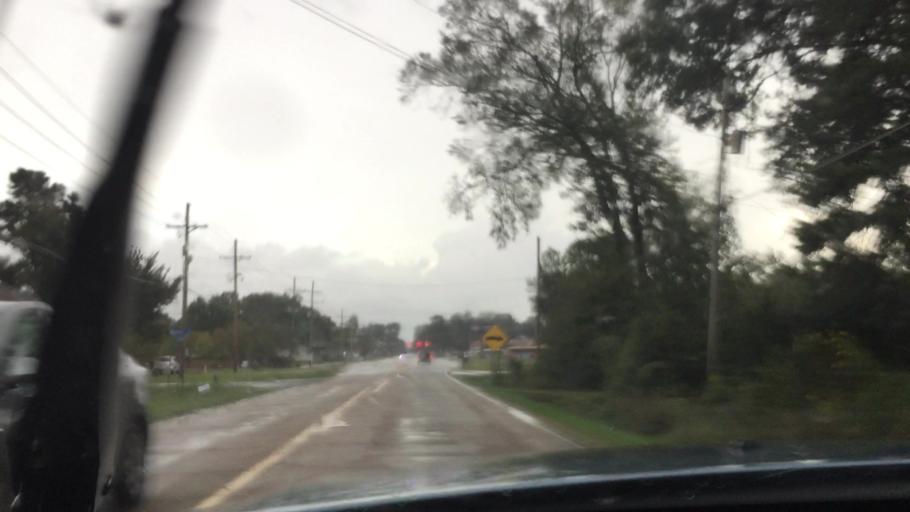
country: US
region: Louisiana
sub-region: East Baton Rouge Parish
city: Monticello
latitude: 30.4498
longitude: -91.0281
